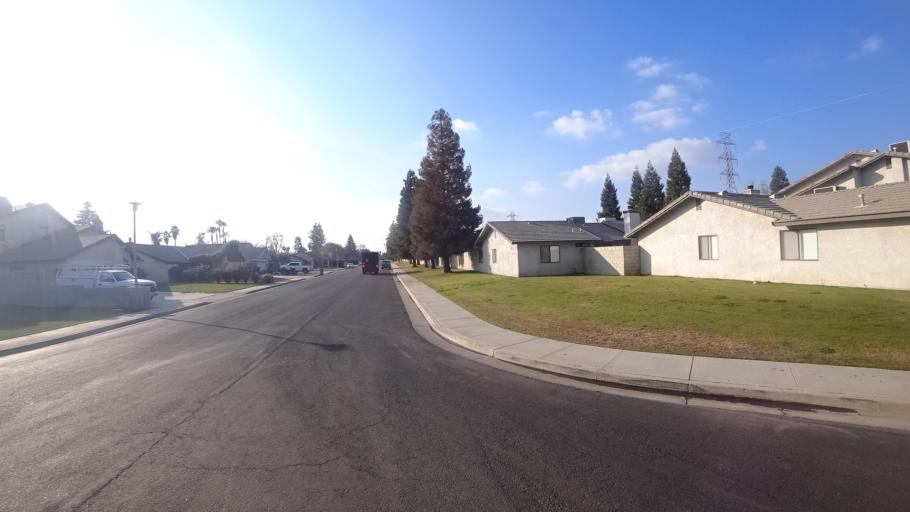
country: US
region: California
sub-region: Kern County
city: Greenacres
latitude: 35.3167
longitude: -119.0929
